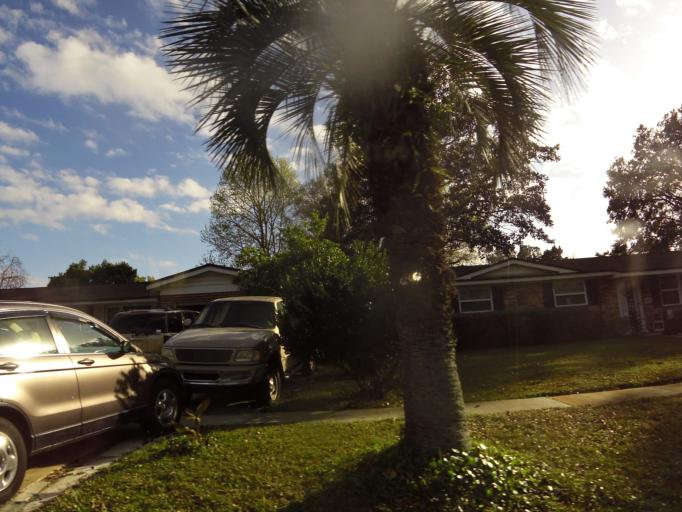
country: US
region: Florida
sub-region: Duval County
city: Jacksonville
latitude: 30.2788
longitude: -81.6047
